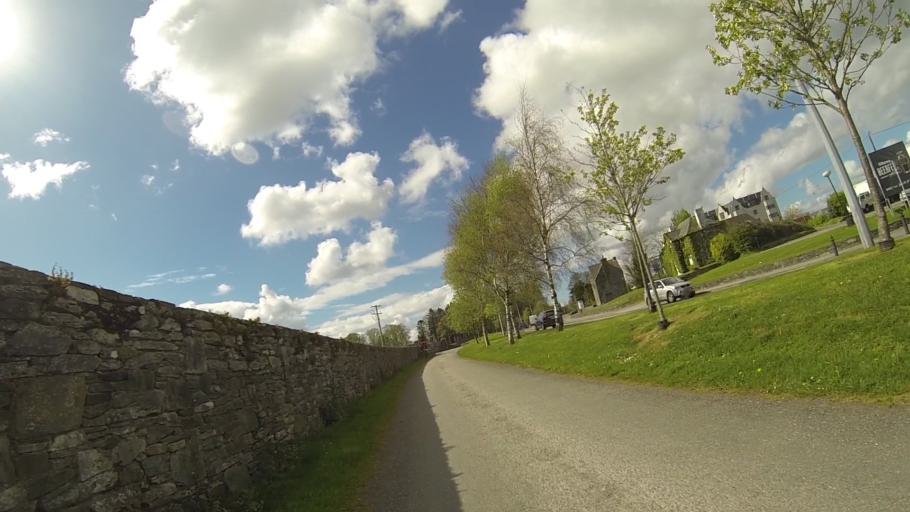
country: IE
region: Munster
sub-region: Ciarrai
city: Cill Airne
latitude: 52.0444
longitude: -9.5037
